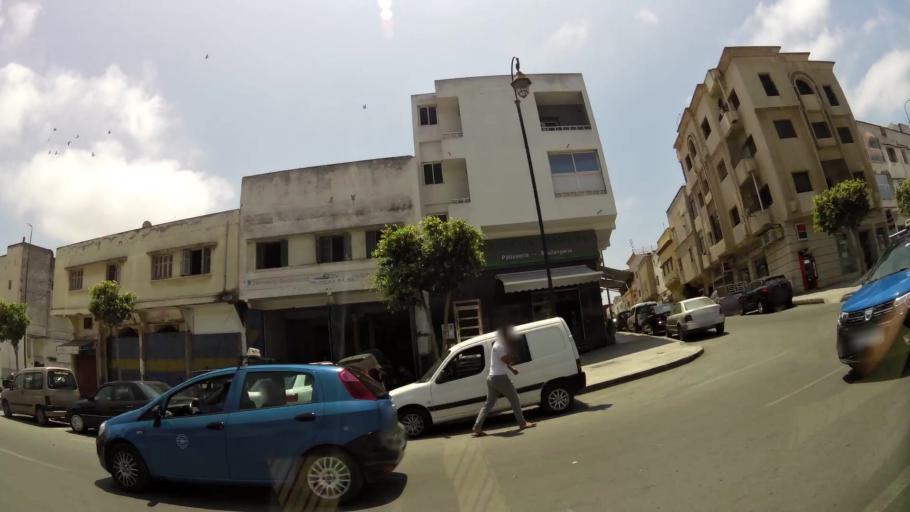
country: MA
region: Rabat-Sale-Zemmour-Zaer
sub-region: Rabat
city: Rabat
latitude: 34.0098
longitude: -6.8570
